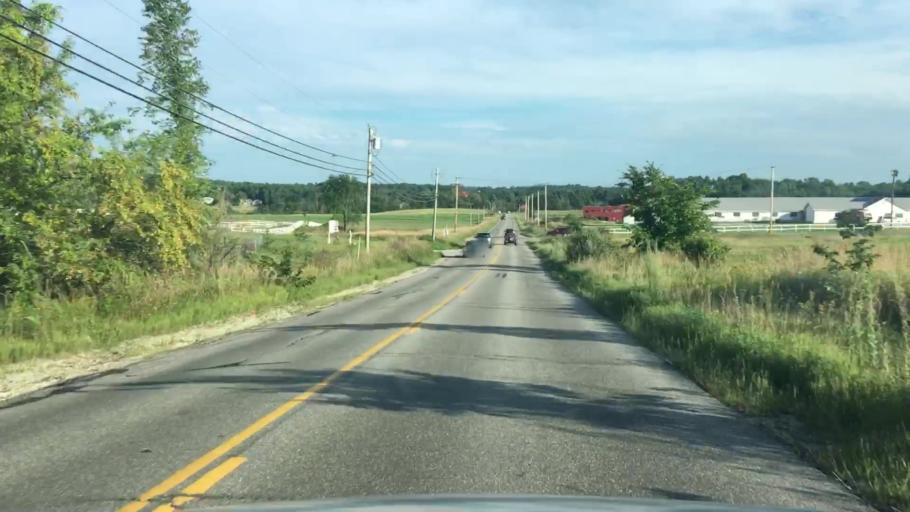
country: US
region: Maine
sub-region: Cumberland County
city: South Windham
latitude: 43.7323
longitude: -70.4123
